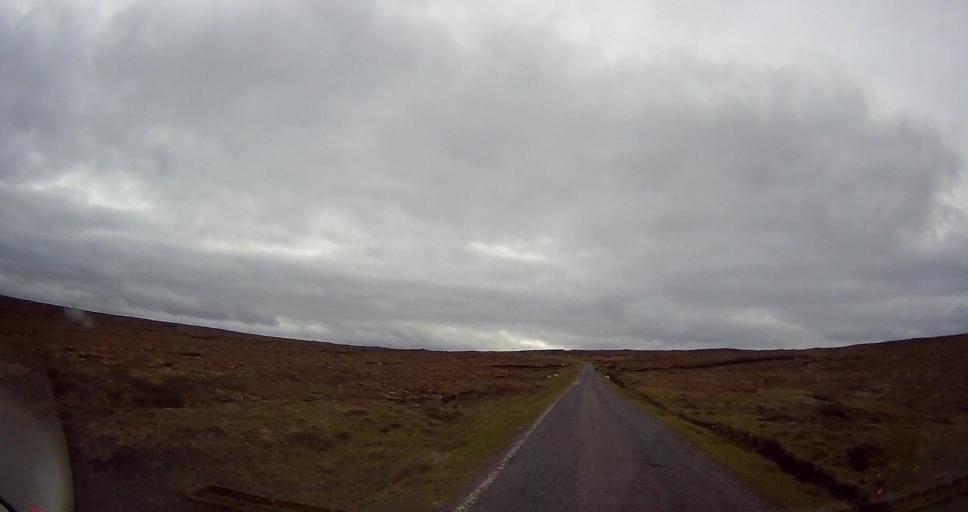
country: GB
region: Scotland
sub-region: Shetland Islands
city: Shetland
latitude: 60.5115
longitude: -1.1203
